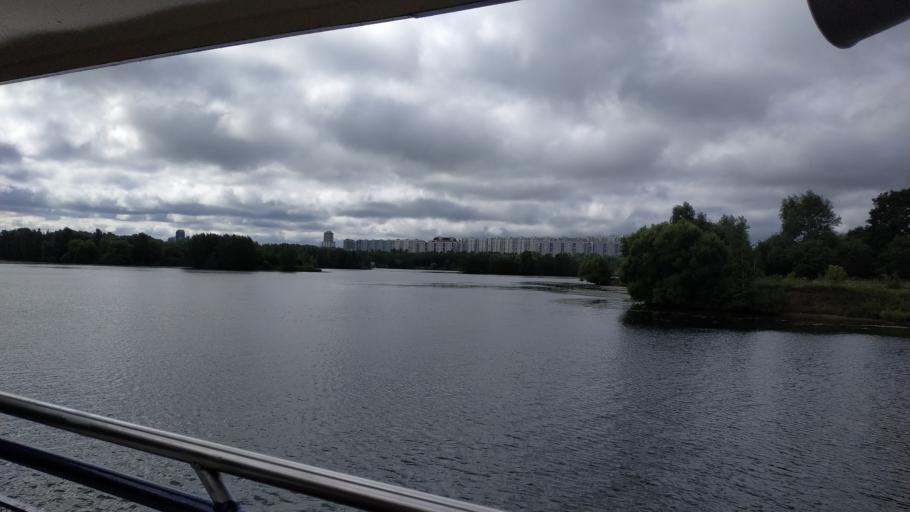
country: RU
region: Moscow
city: Strogino
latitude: 55.8290
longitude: 37.3967
